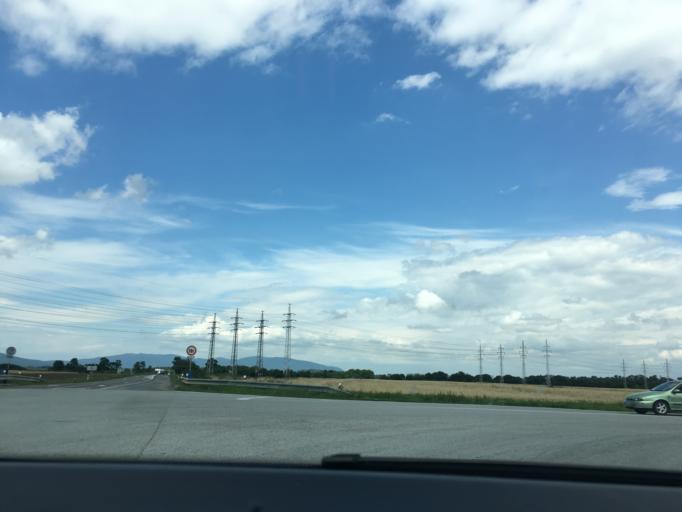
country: SK
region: Kosicky
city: Trebisov
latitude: 48.6332
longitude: 21.6907
